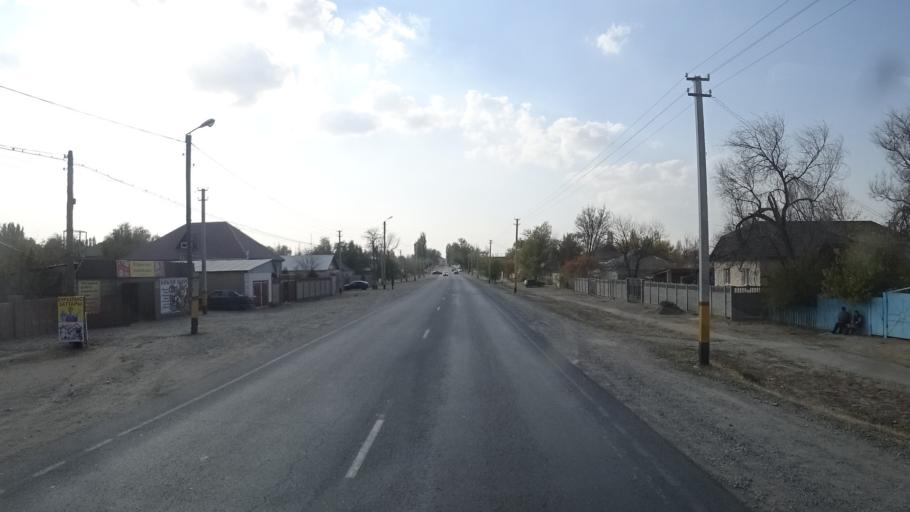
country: KZ
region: Zhambyl
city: Taraz
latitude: 42.8380
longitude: 71.2129
